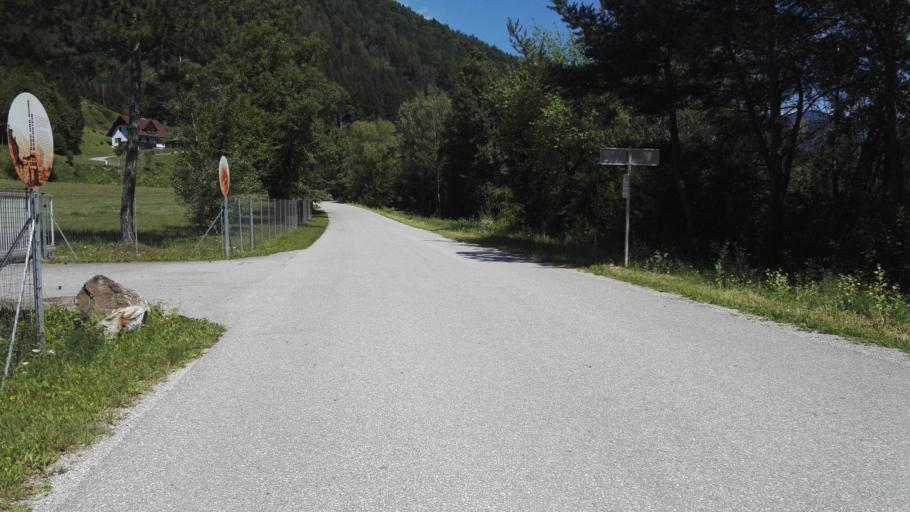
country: AT
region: Styria
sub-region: Politischer Bezirk Graz-Umgebung
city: Frohnleiten
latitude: 47.2478
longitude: 15.3098
